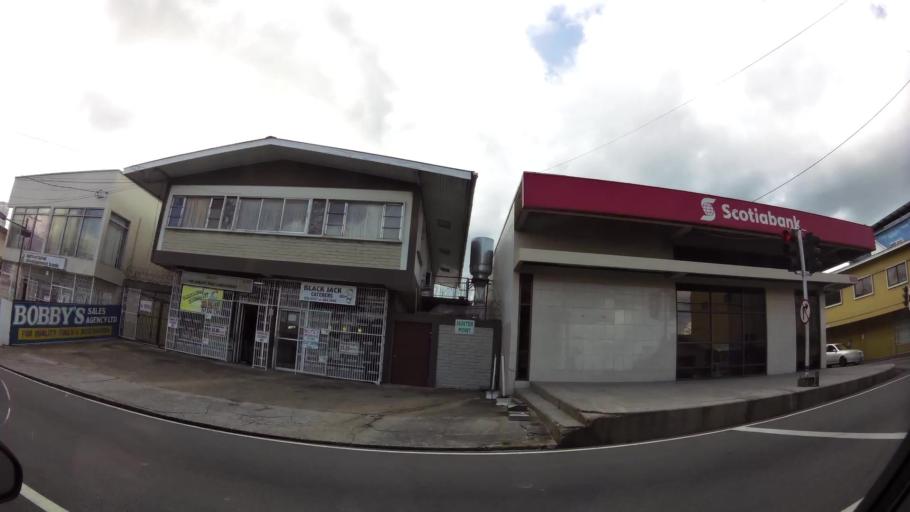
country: TT
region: City of San Fernando
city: San Fernando
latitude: 10.2731
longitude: -61.4611
